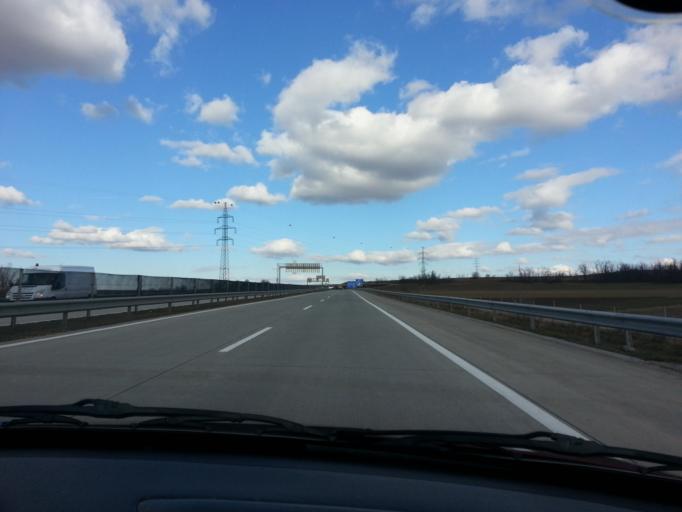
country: HU
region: Pest
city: Nagytarcsa
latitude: 47.5152
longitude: 19.2999
